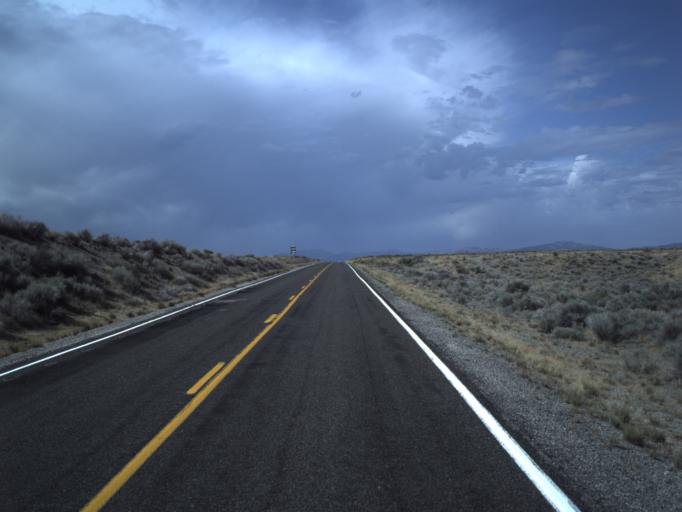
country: US
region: Nevada
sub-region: Elko County
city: West Wendover
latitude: 41.3713
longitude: -114.0289
